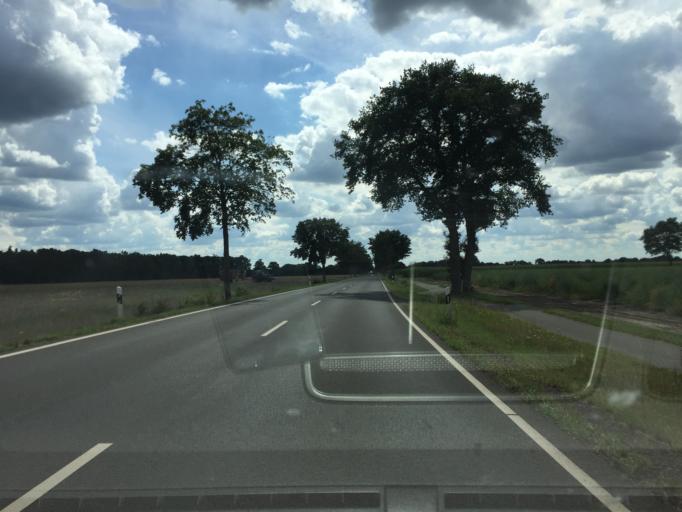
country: DE
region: Lower Saxony
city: Heemsen
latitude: 52.7285
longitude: 9.2921
